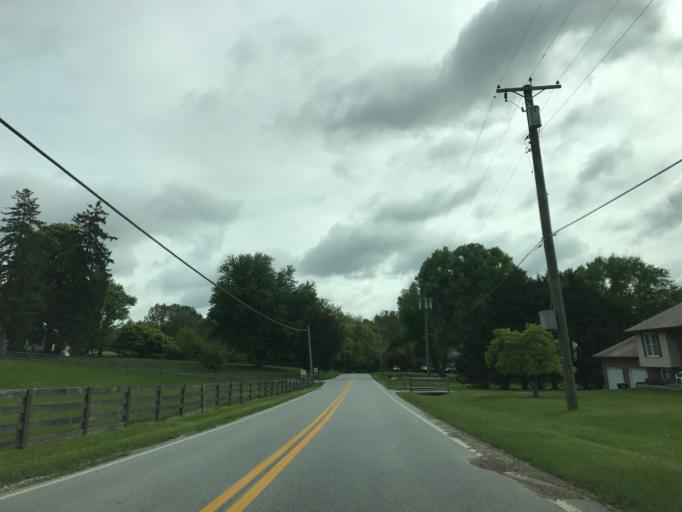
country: US
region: Maryland
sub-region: Carroll County
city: Hampstead
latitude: 39.5349
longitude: -76.9089
